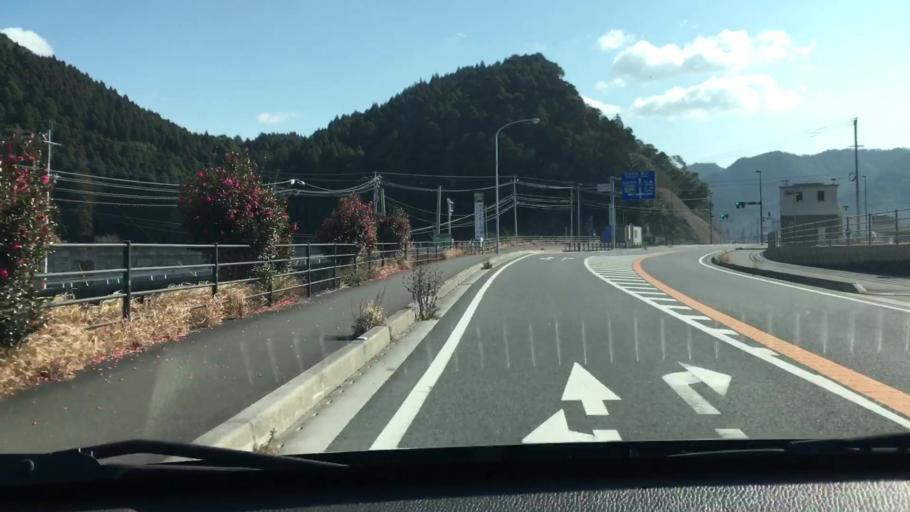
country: JP
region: Oita
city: Saiki
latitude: 32.9585
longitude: 131.8443
